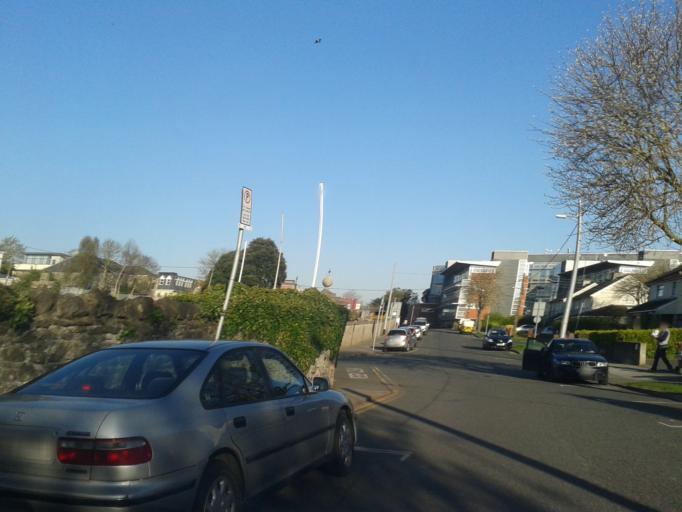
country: IE
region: Leinster
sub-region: Fingal County
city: Swords
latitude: 53.4580
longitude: -6.2169
